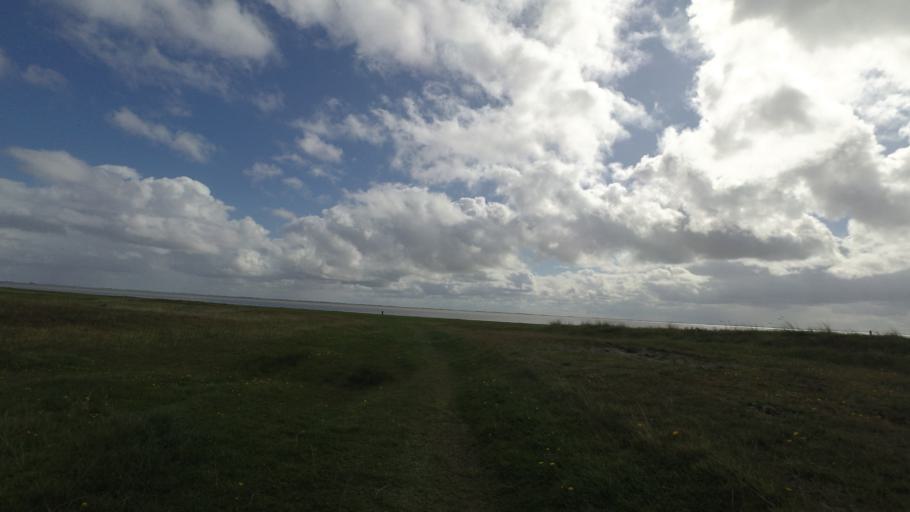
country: NL
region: Friesland
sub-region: Gemeente Ameland
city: Nes
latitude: 53.4471
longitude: 5.8593
